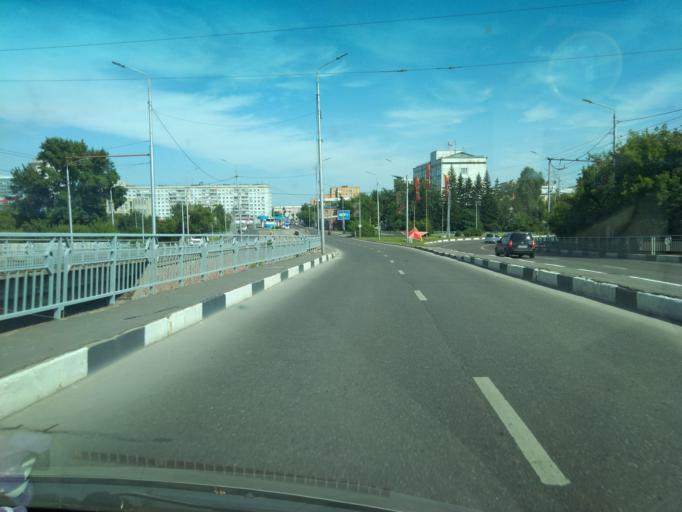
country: RU
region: Krasnoyarskiy
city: Krasnoyarsk
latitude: 56.0124
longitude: 92.8350
